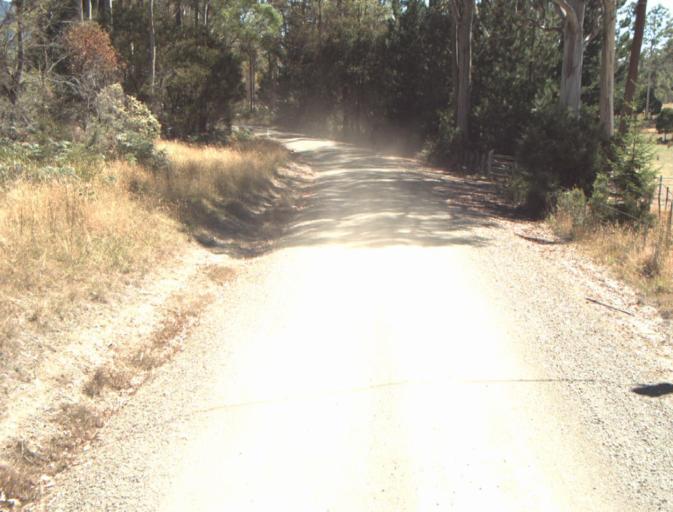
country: AU
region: Tasmania
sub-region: Launceston
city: Newstead
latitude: -41.3434
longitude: 147.3685
